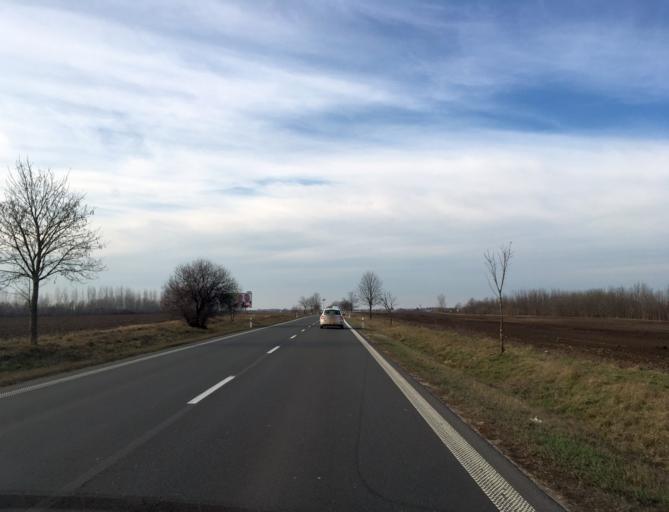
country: SK
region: Nitriansky
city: Surany
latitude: 48.0744
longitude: 18.0864
